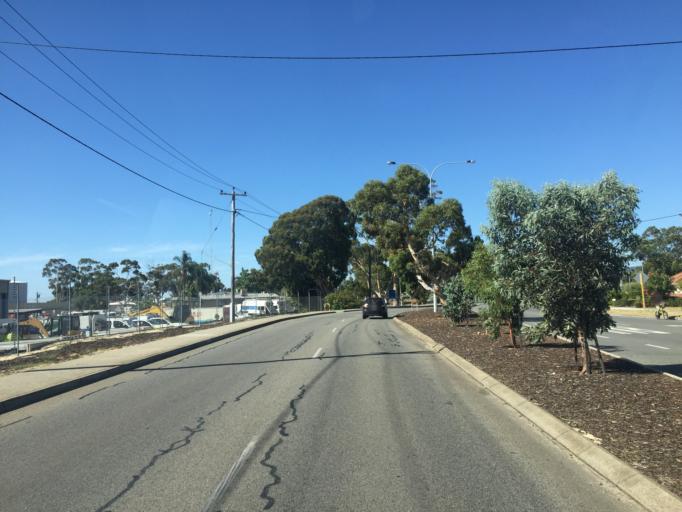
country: AU
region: Western Australia
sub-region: Gosnells
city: Maddington
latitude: -32.0497
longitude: 115.9847
